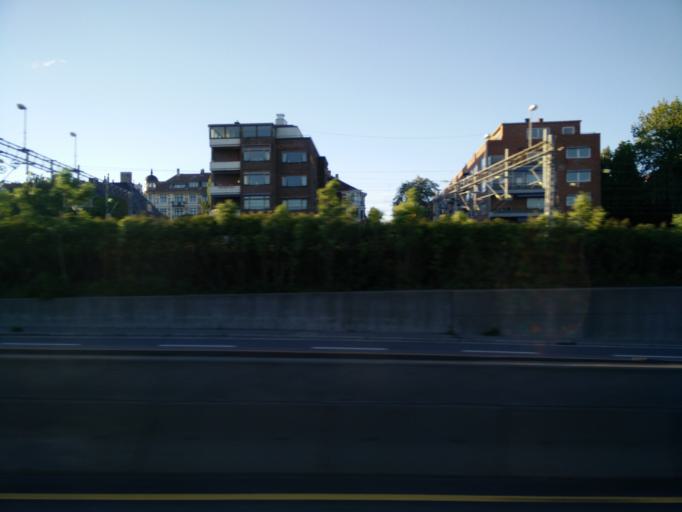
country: NO
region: Oslo
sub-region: Oslo
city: Sjolyststranda
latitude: 59.9107
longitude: 10.7069
